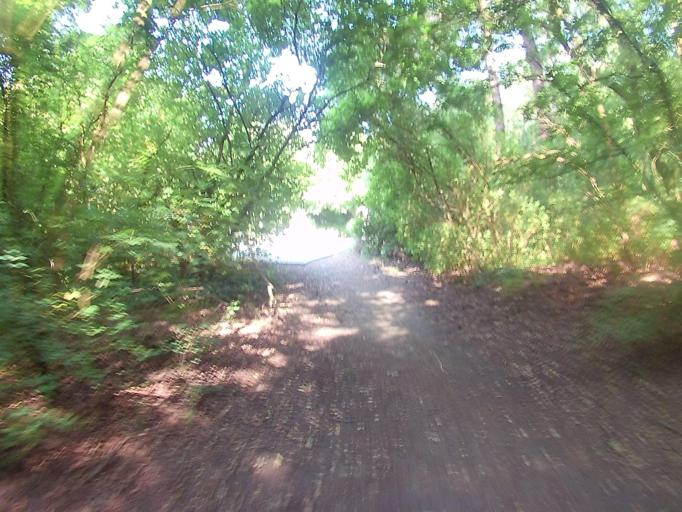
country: DE
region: Berlin
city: Grunau
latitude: 52.4086
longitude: 13.5925
